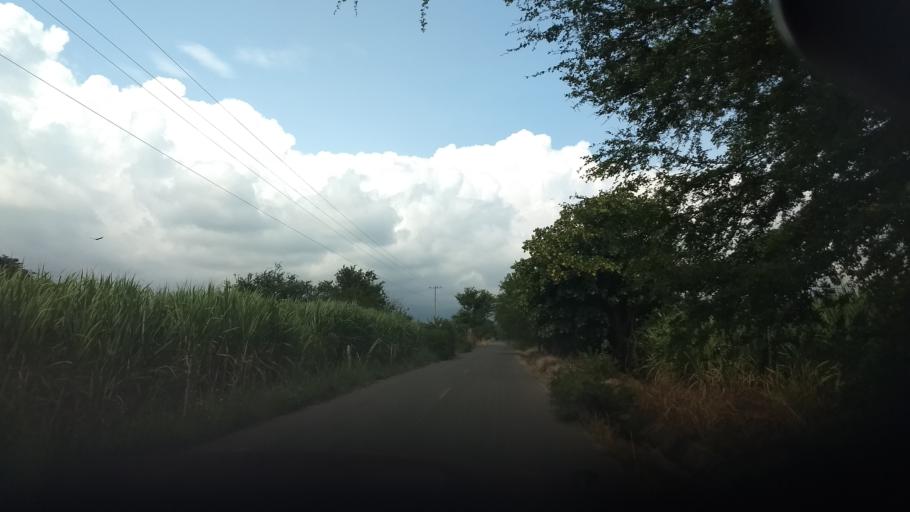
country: MX
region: Jalisco
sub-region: Tonila
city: San Marcos
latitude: 19.4255
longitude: -103.4910
